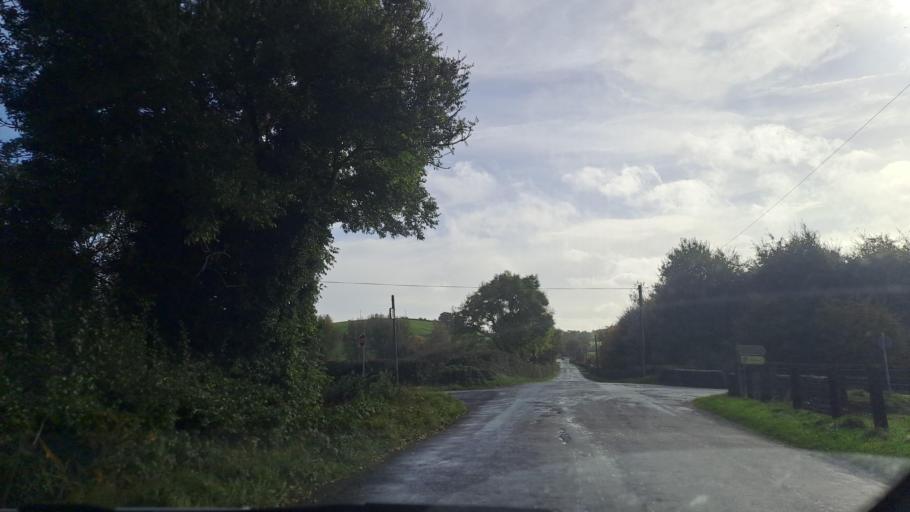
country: IE
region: Ulster
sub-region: County Monaghan
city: Carrickmacross
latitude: 53.8987
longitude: -6.6953
